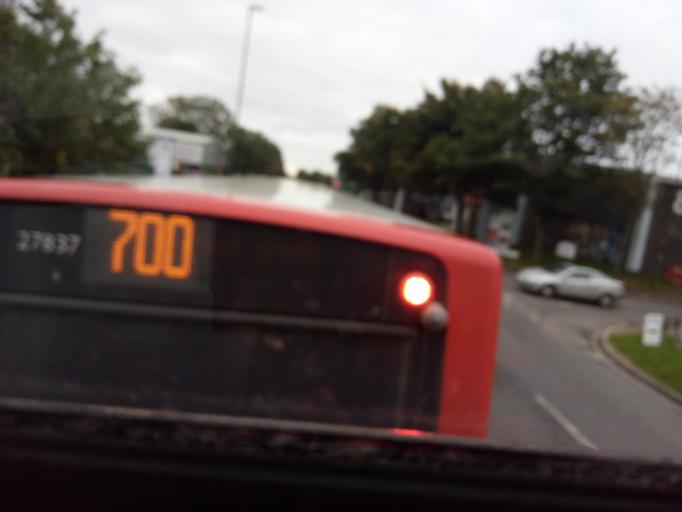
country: GB
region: England
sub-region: West Sussex
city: Chichester
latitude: 50.8312
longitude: -0.7564
